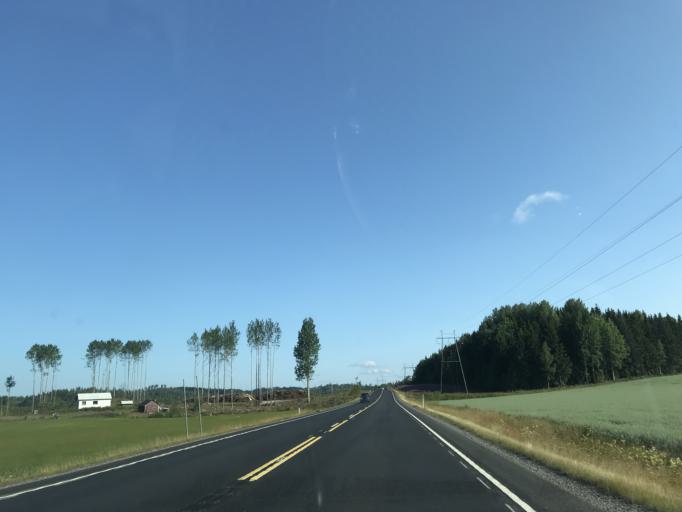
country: FI
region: Paijanne Tavastia
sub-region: Lahti
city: Lahti
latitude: 61.1125
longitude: 25.6418
